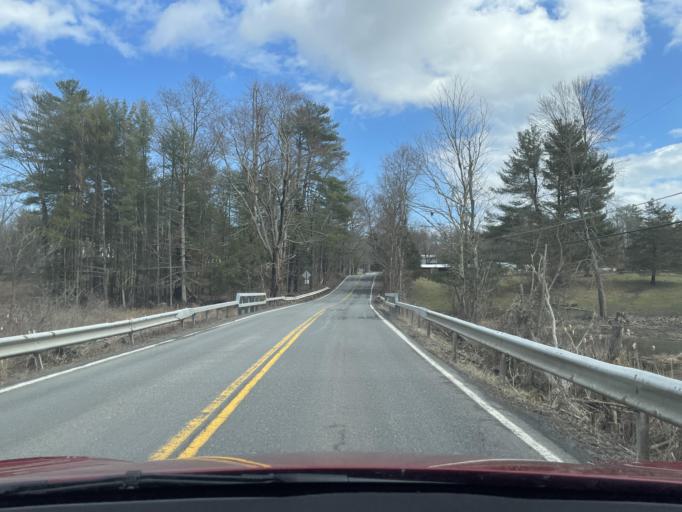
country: US
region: New York
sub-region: Ulster County
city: Zena
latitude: 42.0462
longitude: -74.0451
